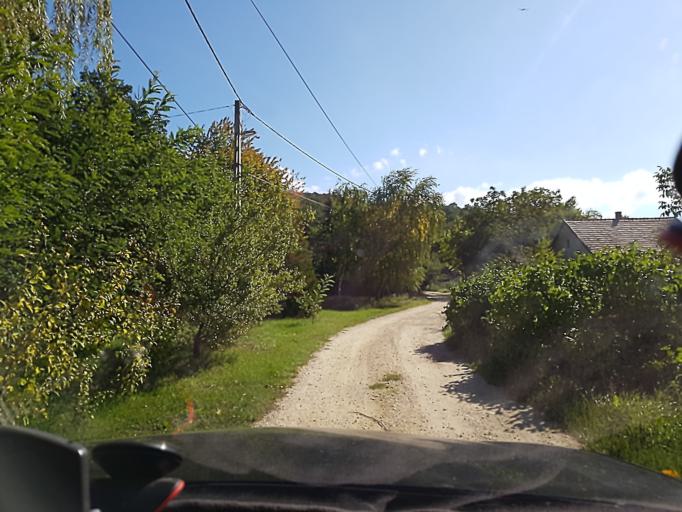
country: HU
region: Pest
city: Piliscsaba
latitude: 47.6352
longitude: 18.8492
